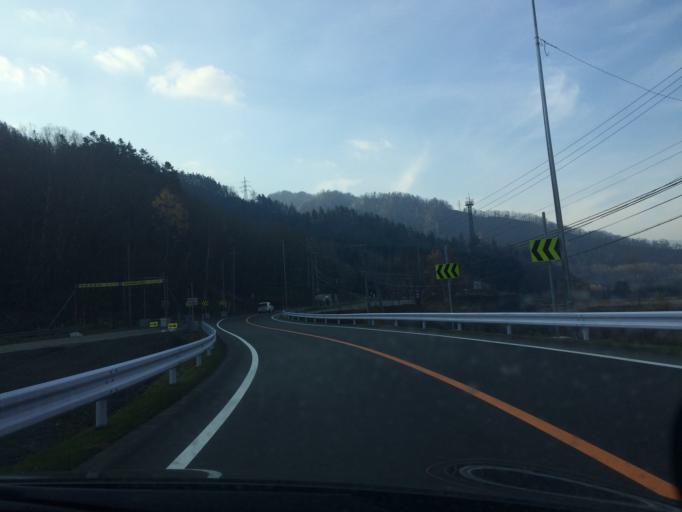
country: JP
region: Hokkaido
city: Shimo-furano
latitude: 42.9108
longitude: 142.5851
